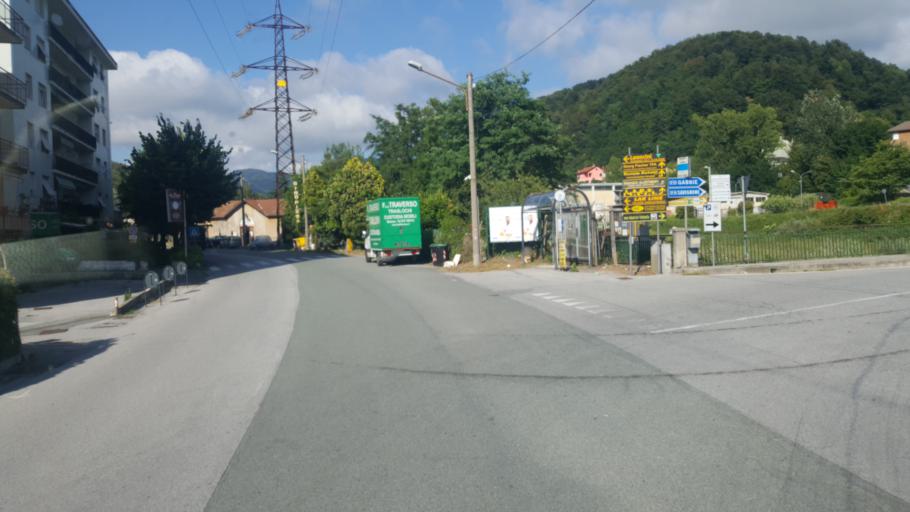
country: IT
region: Liguria
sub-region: Provincia di Genova
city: Busalla
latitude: 44.5721
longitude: 8.9588
